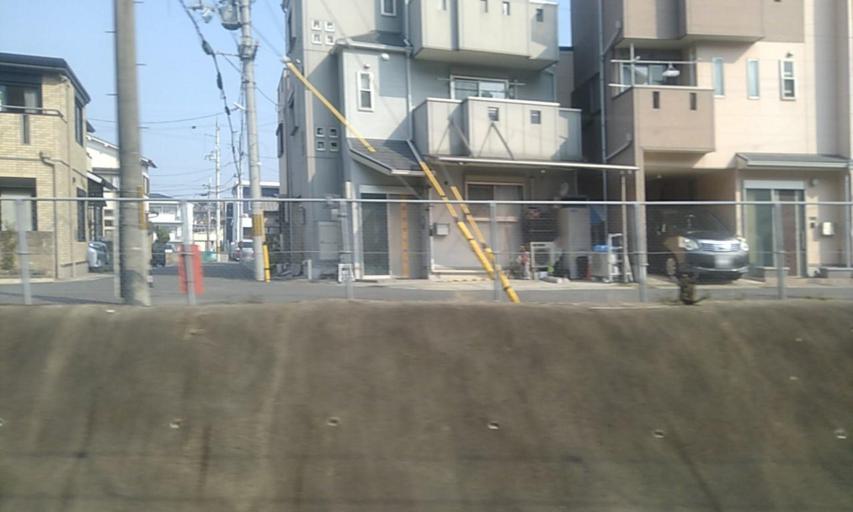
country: JP
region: Kyoto
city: Uji
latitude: 34.8889
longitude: 135.7915
